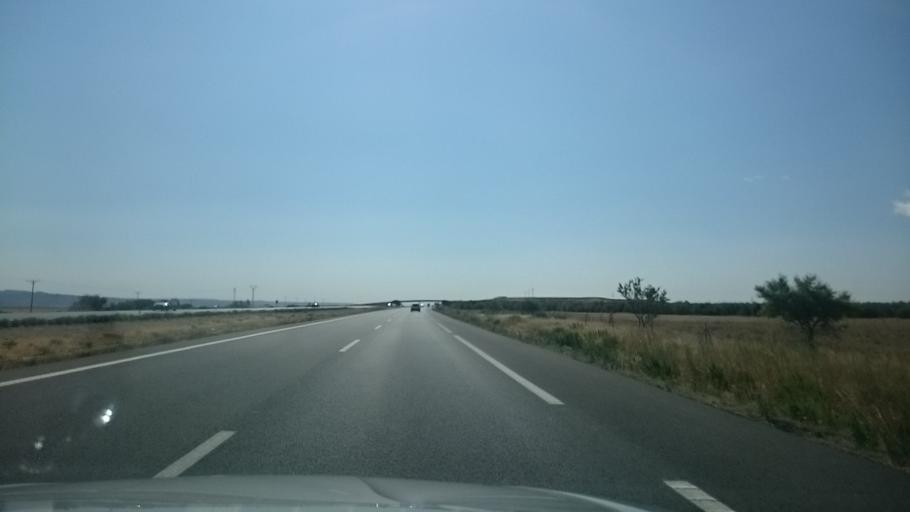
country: ES
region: Aragon
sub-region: Provincia de Zaragoza
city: Gallur
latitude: 41.8428
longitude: -1.3501
